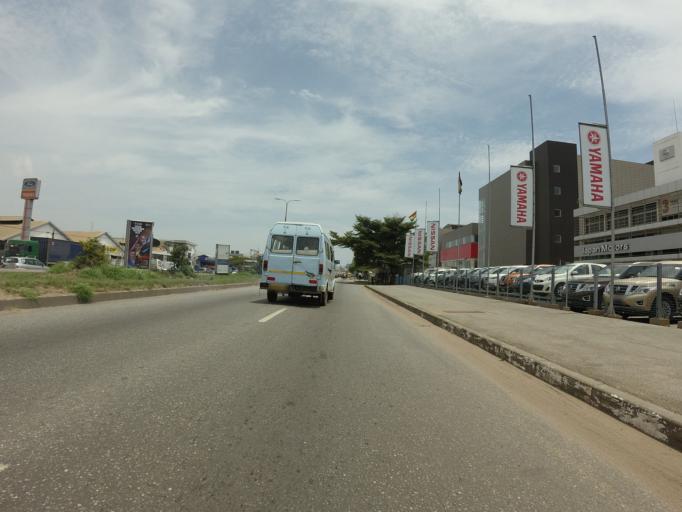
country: GH
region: Greater Accra
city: Accra
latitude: 5.5586
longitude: -0.2249
